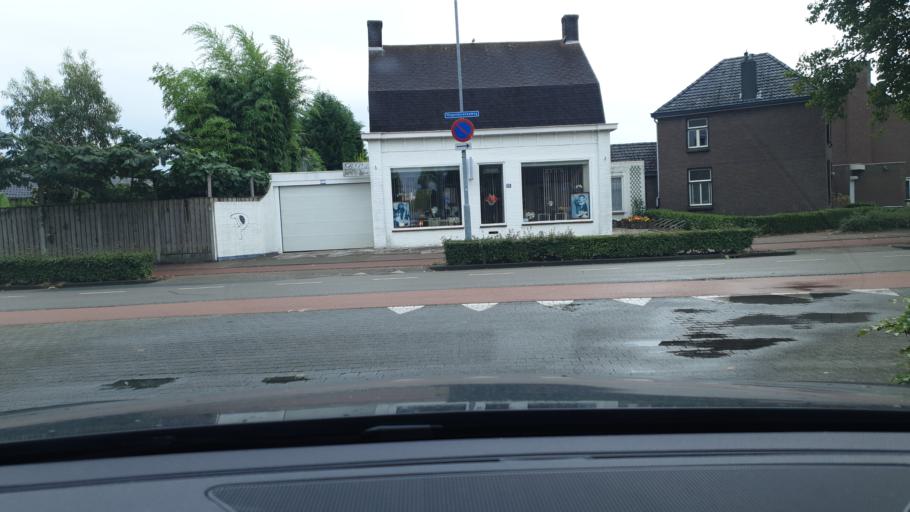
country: NL
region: North Brabant
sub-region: Gemeente Veldhoven
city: Veldhoven
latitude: 51.4188
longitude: 5.4135
